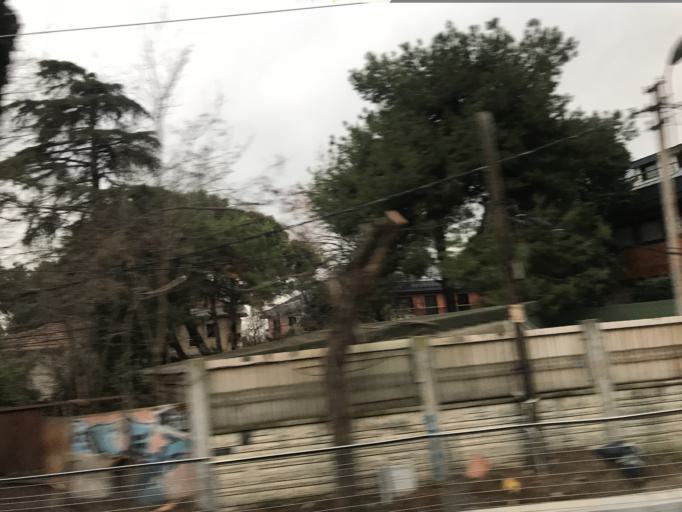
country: TR
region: Istanbul
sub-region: Atasehir
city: Atasehir
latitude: 40.9416
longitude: 29.1118
